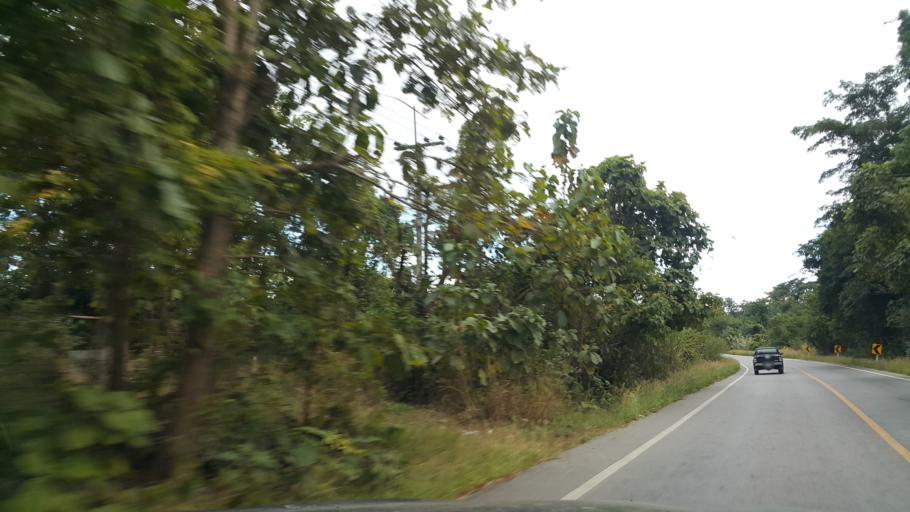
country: TH
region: Lampang
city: Thoen
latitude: 17.5599
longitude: 99.3335
